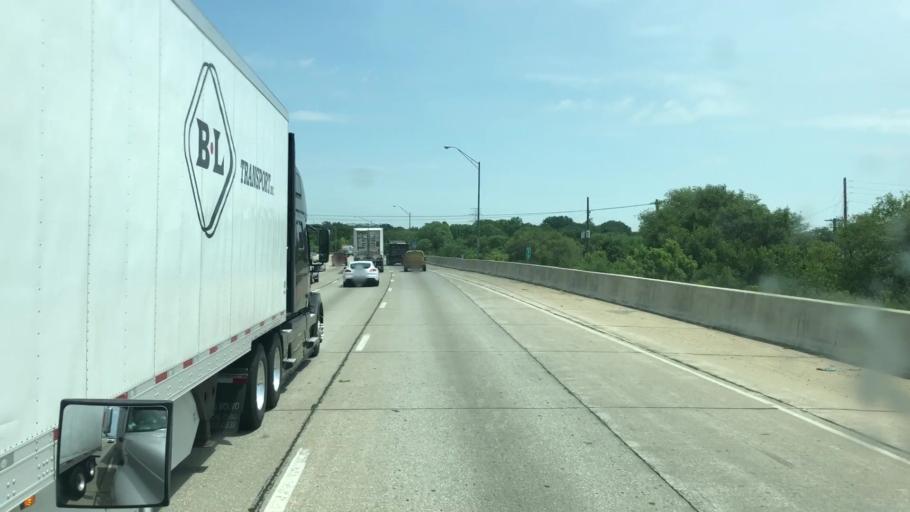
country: US
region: Indiana
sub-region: Marion County
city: Indianapolis
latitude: 39.7530
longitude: -86.2175
